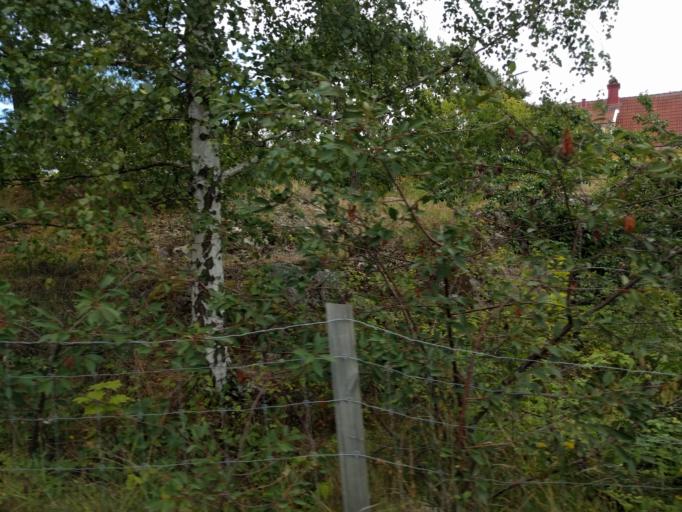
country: SE
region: Soedermanland
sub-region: Oxelosunds Kommun
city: Bara
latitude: 58.4936
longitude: 16.9352
